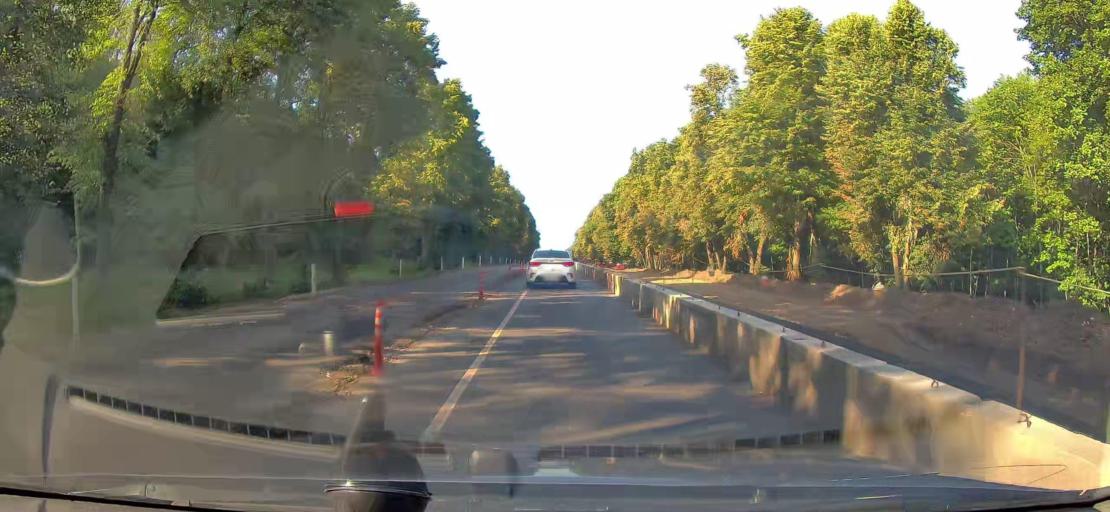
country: RU
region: Orjol
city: Spasskoye-Lutovinovo
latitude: 53.3607
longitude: 36.7238
